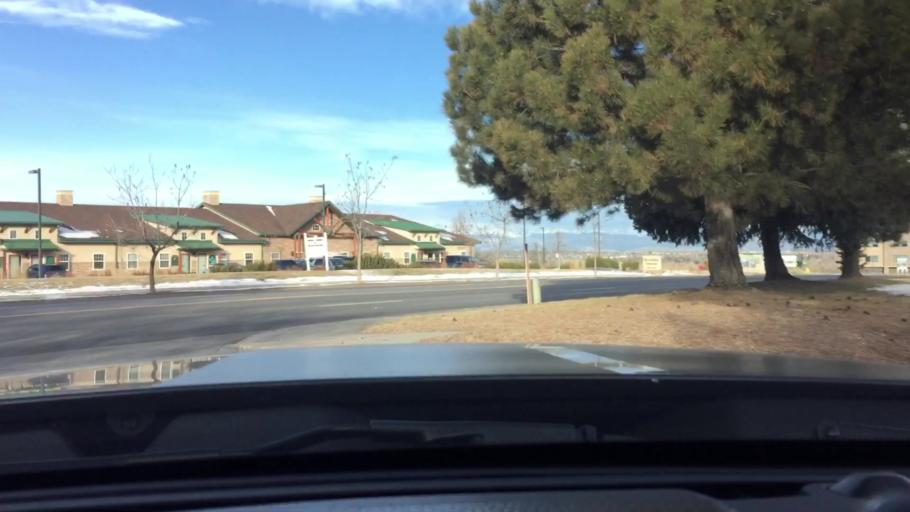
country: US
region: Colorado
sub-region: Adams County
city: Northglenn
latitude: 39.9191
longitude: -105.0047
